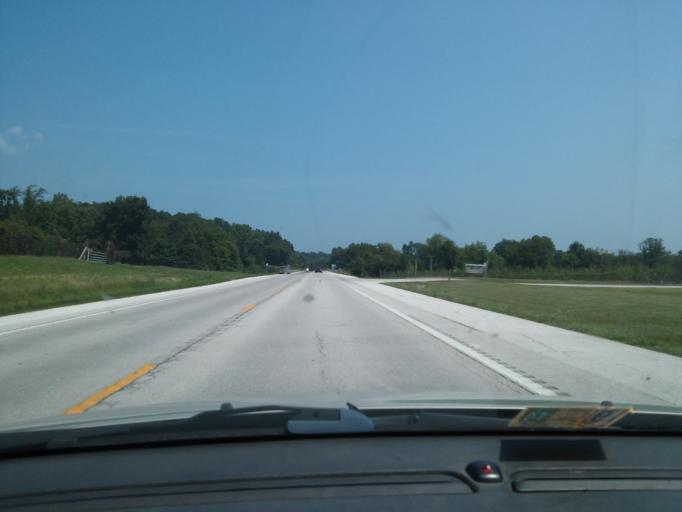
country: US
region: Missouri
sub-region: Pike County
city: Louisiana
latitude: 39.4279
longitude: -91.0832
